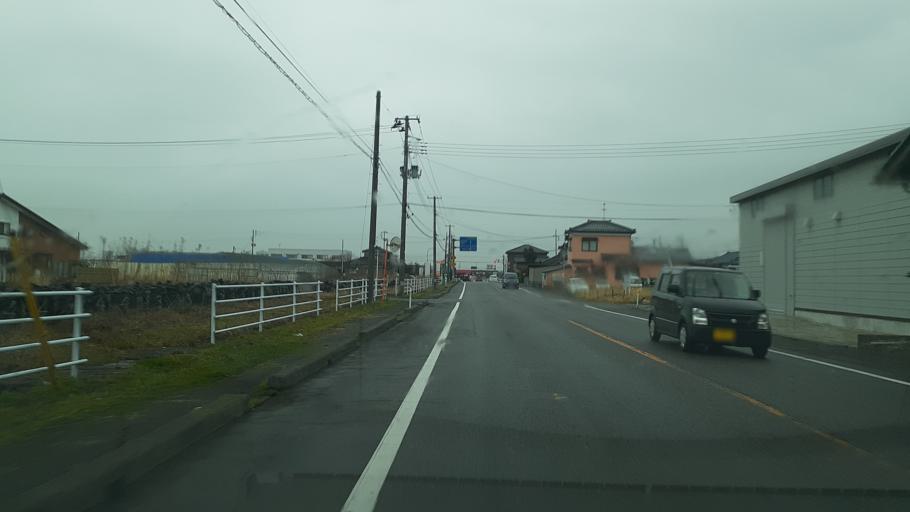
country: JP
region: Niigata
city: Kameda-honcho
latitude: 37.8795
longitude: 139.1255
